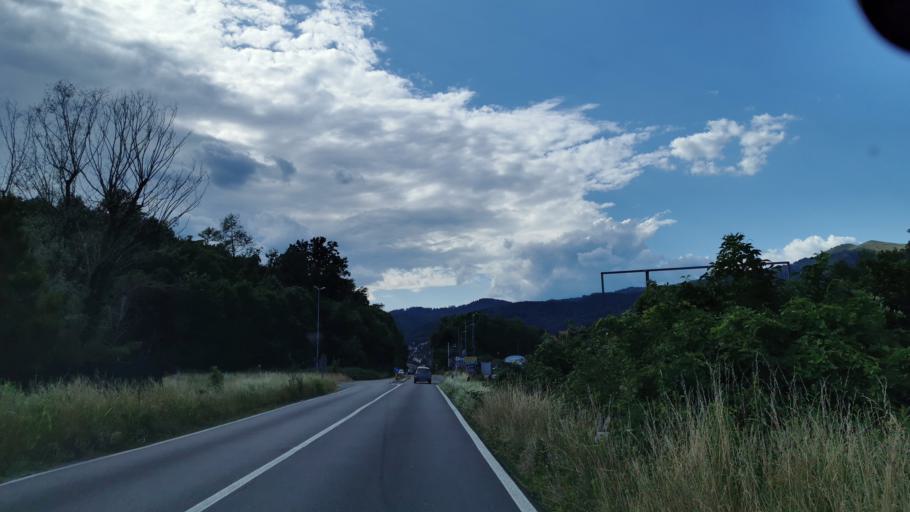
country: IT
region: Lombardy
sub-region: Provincia di Como
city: Albese Con Cassano
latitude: 45.7906
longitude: 9.1554
